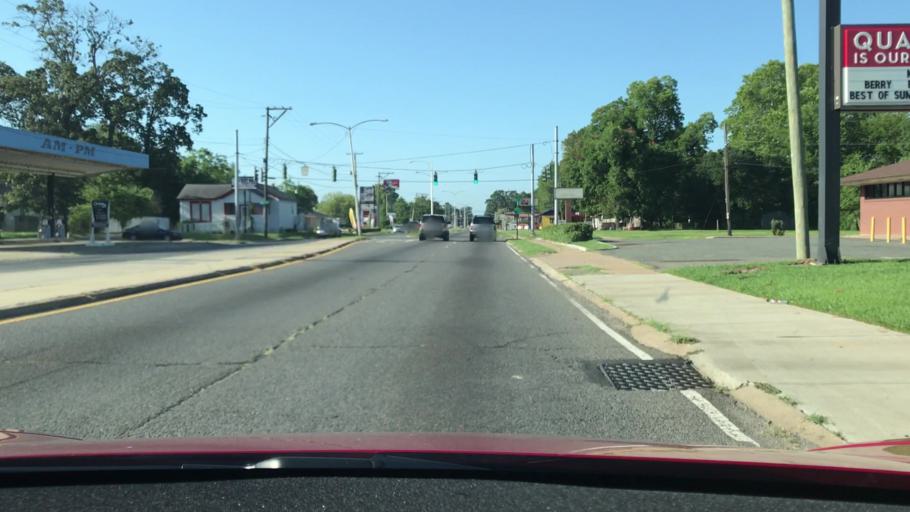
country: US
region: Louisiana
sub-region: Caddo Parish
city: Shreveport
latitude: 32.4771
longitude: -93.7801
